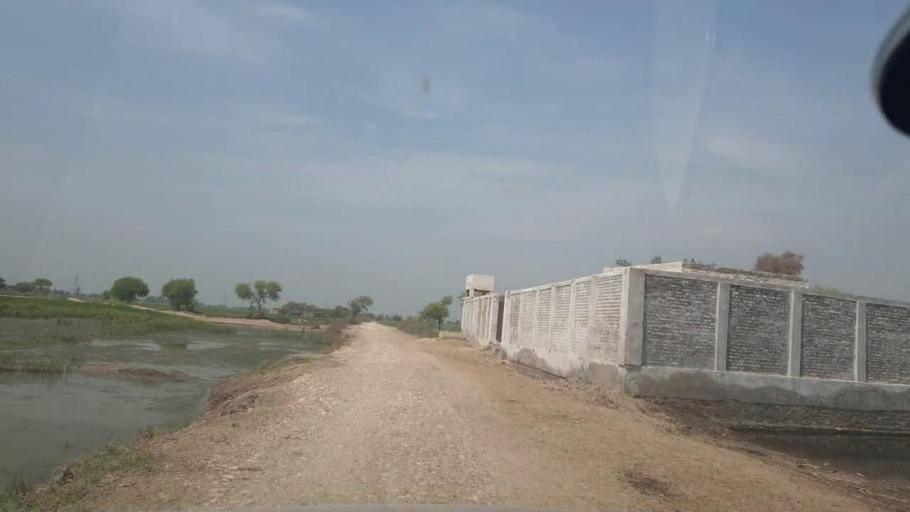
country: PK
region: Sindh
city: Thul
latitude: 28.1743
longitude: 68.6265
